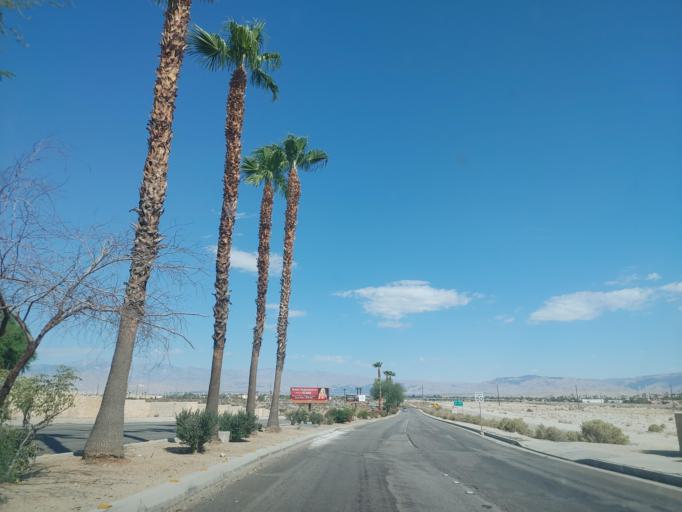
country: US
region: California
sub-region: Riverside County
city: Cathedral City
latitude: 33.8034
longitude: -116.4761
